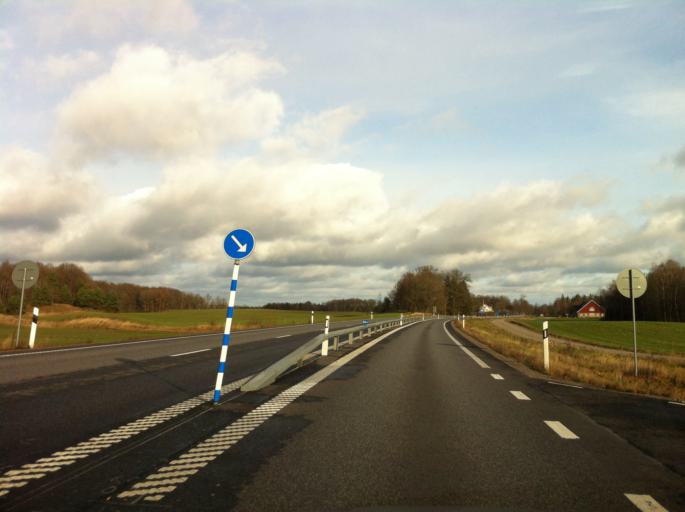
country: SE
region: Kronoberg
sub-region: Alvesta Kommun
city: Vislanda
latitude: 56.7023
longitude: 14.3793
